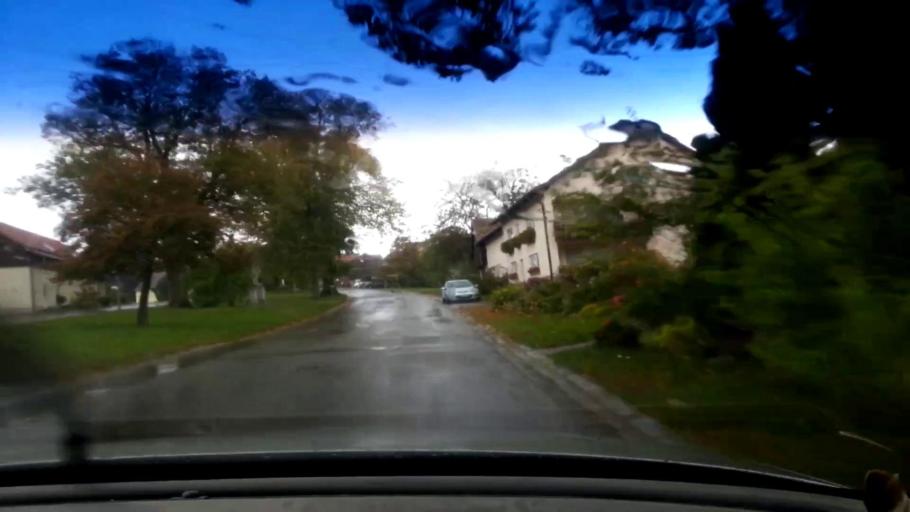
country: DE
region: Bavaria
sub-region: Upper Franconia
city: Stadelhofen
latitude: 50.0421
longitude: 11.2048
